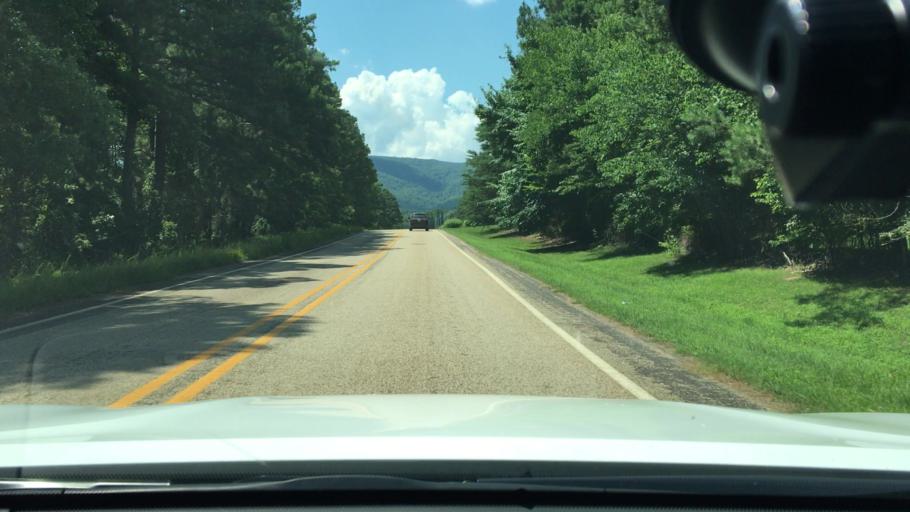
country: US
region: Arkansas
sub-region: Logan County
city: Paris
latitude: 35.2079
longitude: -93.6346
